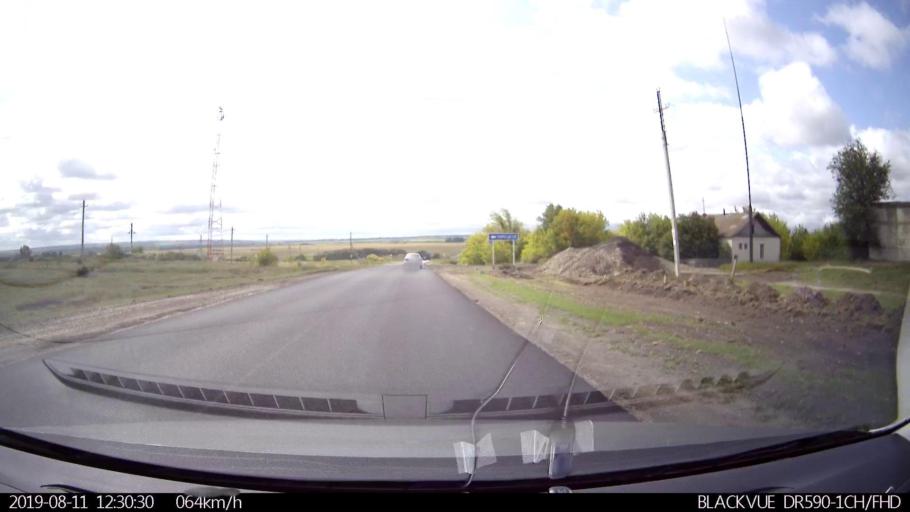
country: RU
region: Ulyanovsk
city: Ignatovka
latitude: 53.8253
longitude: 47.8937
